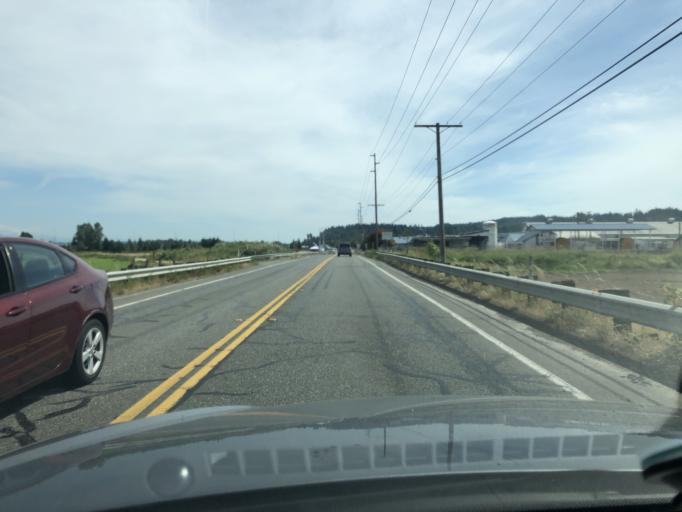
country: US
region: Washington
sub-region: King County
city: Kent
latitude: 47.3574
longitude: -122.2494
